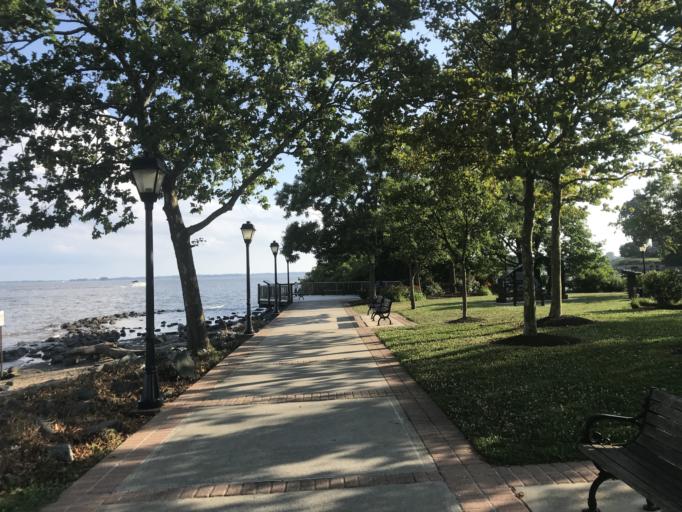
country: US
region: Maryland
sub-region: Harford County
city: Havre de Grace
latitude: 39.5400
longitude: -76.0848
